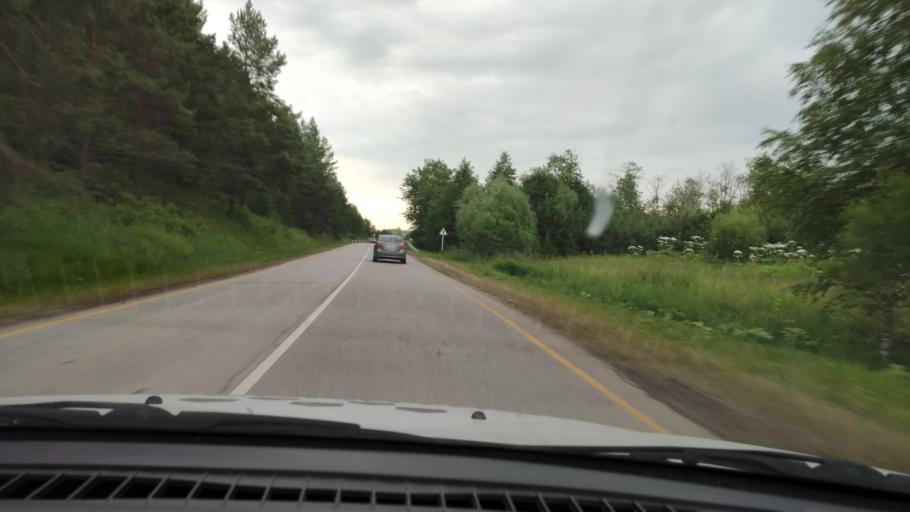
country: RU
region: Perm
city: Kukushtan
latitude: 57.4927
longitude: 56.6398
